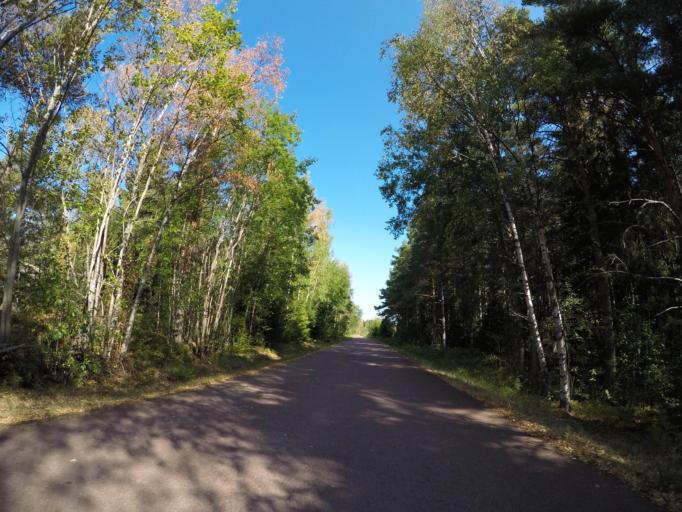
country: AX
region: Alands landsbygd
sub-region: Finstroem
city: Finstroem
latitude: 60.2763
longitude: 19.9179
